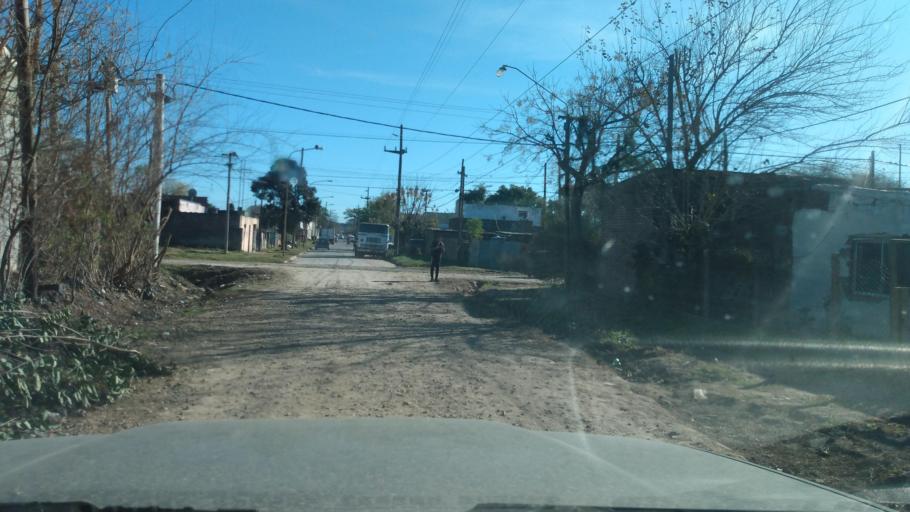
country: AR
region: Buenos Aires
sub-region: Partido de Lujan
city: Lujan
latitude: -34.5708
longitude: -59.1290
